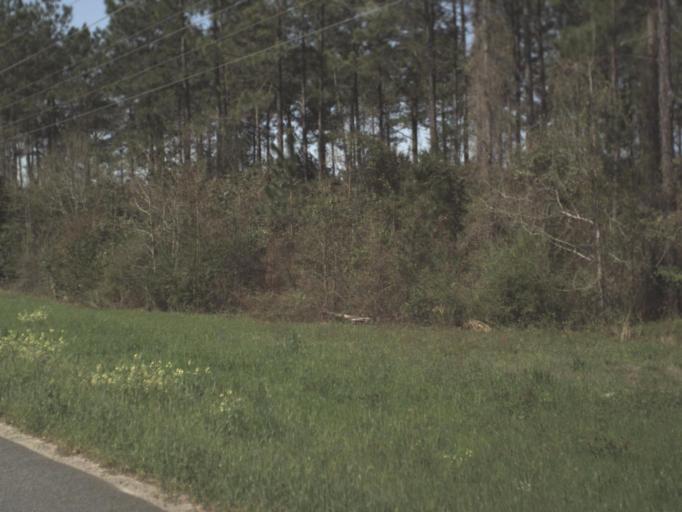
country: US
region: Florida
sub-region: Jackson County
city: Graceville
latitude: 30.9448
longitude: -85.4072
